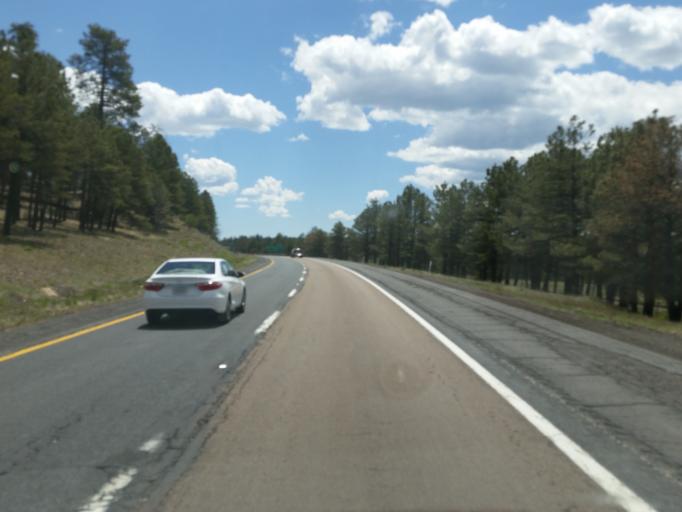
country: US
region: Arizona
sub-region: Coconino County
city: Flagstaff
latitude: 35.2037
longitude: -111.7671
